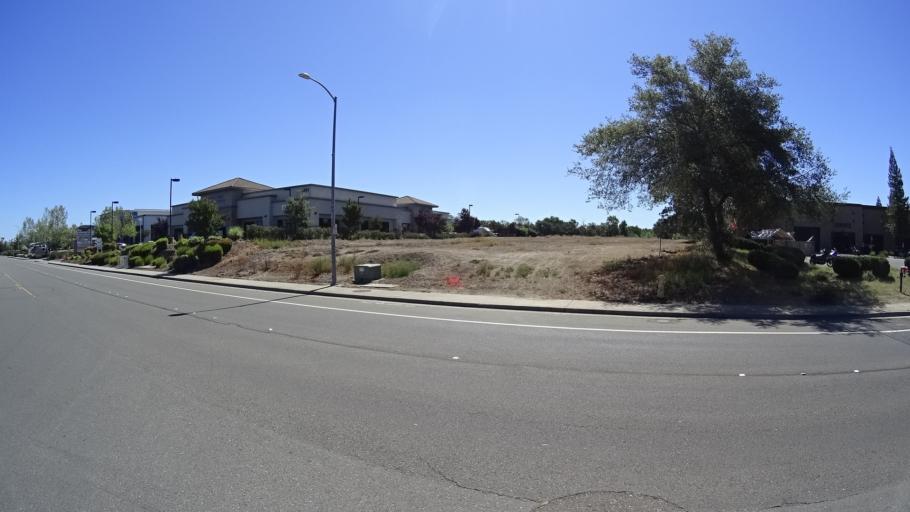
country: US
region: California
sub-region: Placer County
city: Rocklin
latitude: 38.7993
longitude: -121.2130
